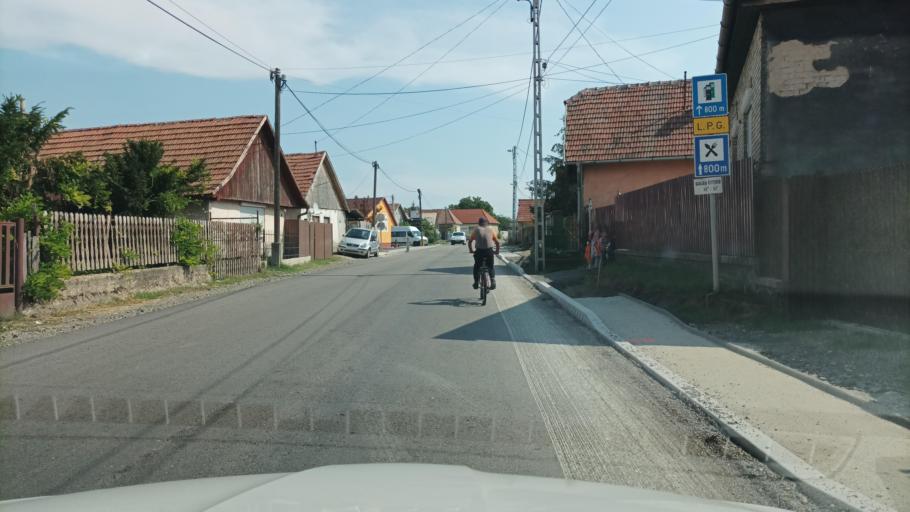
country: HU
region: Pest
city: Tura
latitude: 47.6088
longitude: 19.5931
